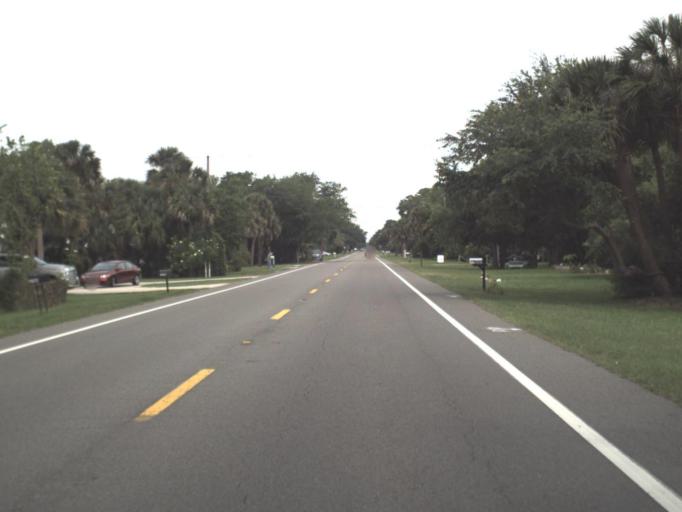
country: US
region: Florida
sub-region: Duval County
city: Atlantic Beach
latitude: 30.4112
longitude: -81.5178
